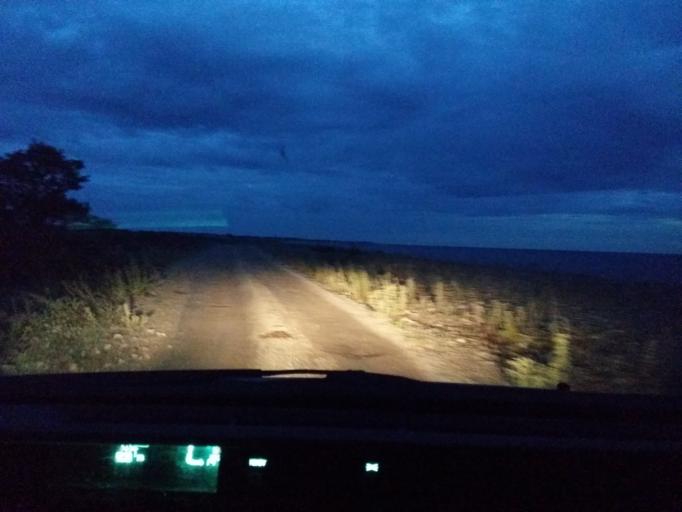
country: SE
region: Kalmar
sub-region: Borgholms Kommun
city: Borgholm
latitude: 57.1275
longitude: 16.9005
